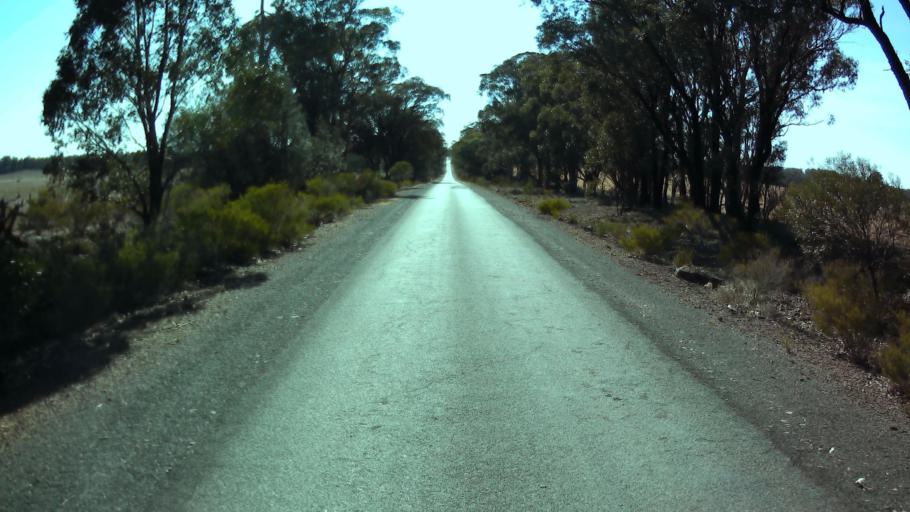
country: AU
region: New South Wales
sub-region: Weddin
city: Grenfell
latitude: -33.7835
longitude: 147.9750
